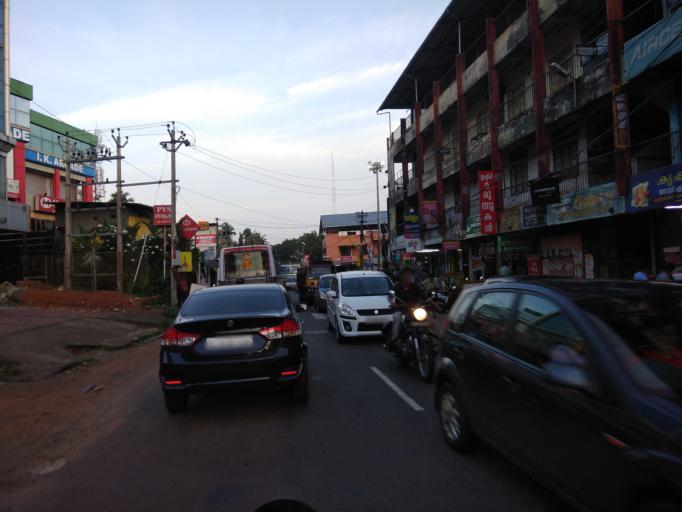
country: IN
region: Kerala
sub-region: Thrissur District
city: Trichur
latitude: 10.5282
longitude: 76.1867
